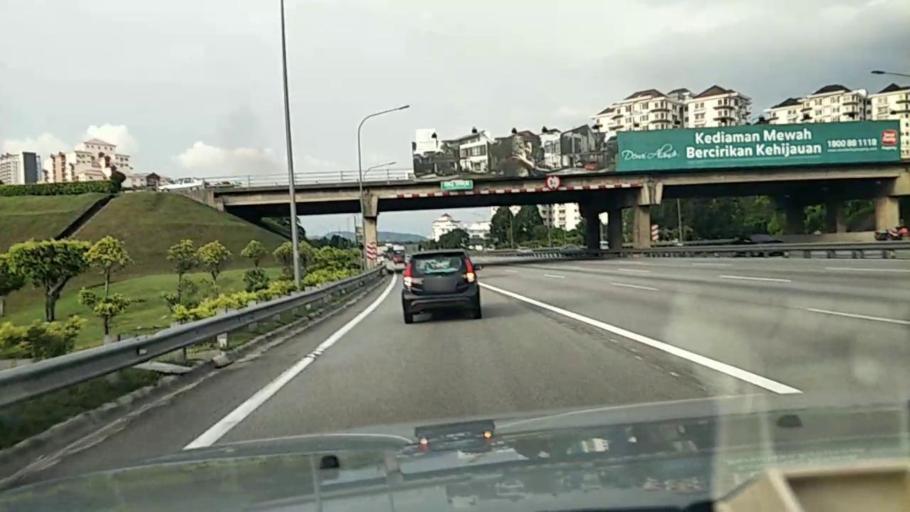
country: MY
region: Selangor
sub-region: Petaling
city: Petaling Jaya
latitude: 3.1061
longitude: 101.5896
